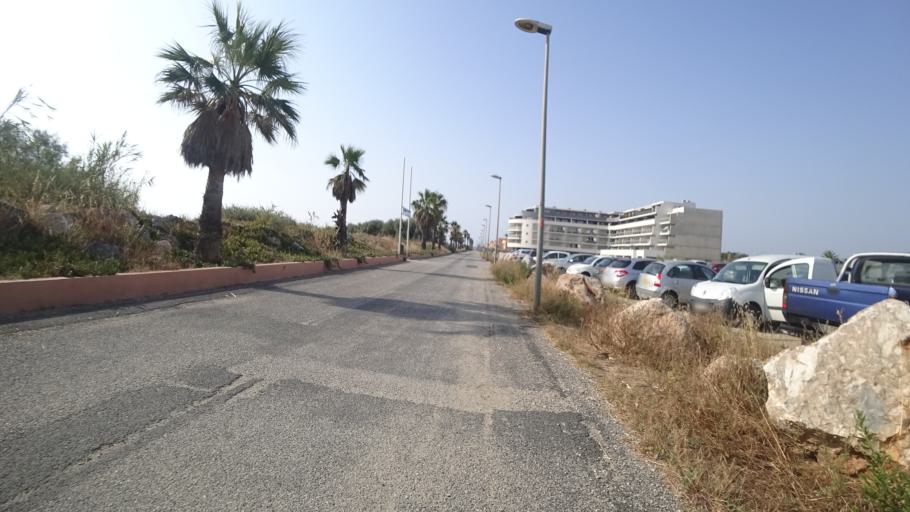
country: FR
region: Languedoc-Roussillon
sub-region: Departement des Pyrenees-Orientales
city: Sainte-Marie-Plage
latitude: 42.7385
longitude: 3.0366
